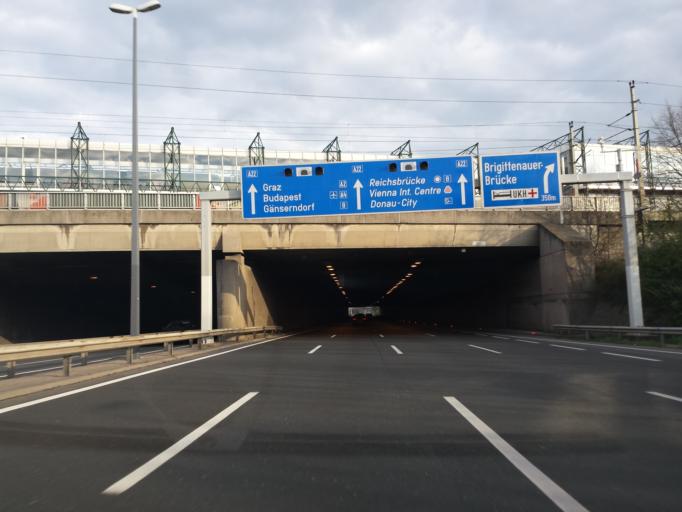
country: AT
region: Vienna
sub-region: Wien Stadt
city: Vienna
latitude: 48.2472
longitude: 16.3944
